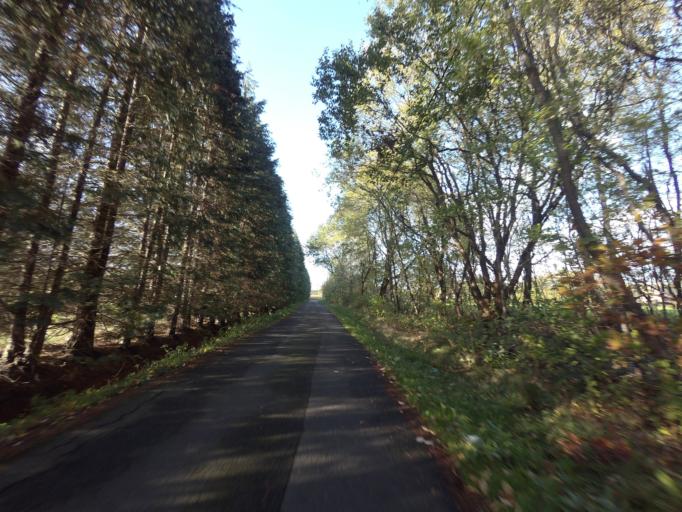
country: BE
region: Flanders
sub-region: Provincie Antwerpen
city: Bonheiden
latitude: 51.0272
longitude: 4.5783
